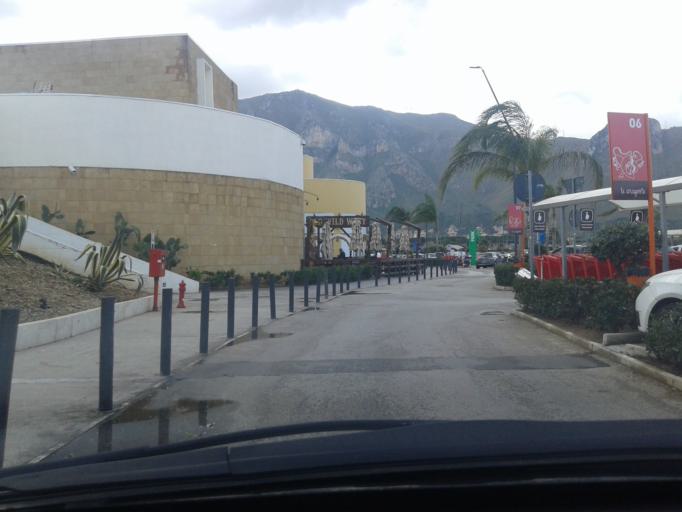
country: IT
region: Sicily
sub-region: Palermo
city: Ciaculli
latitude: 38.0895
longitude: 13.4118
